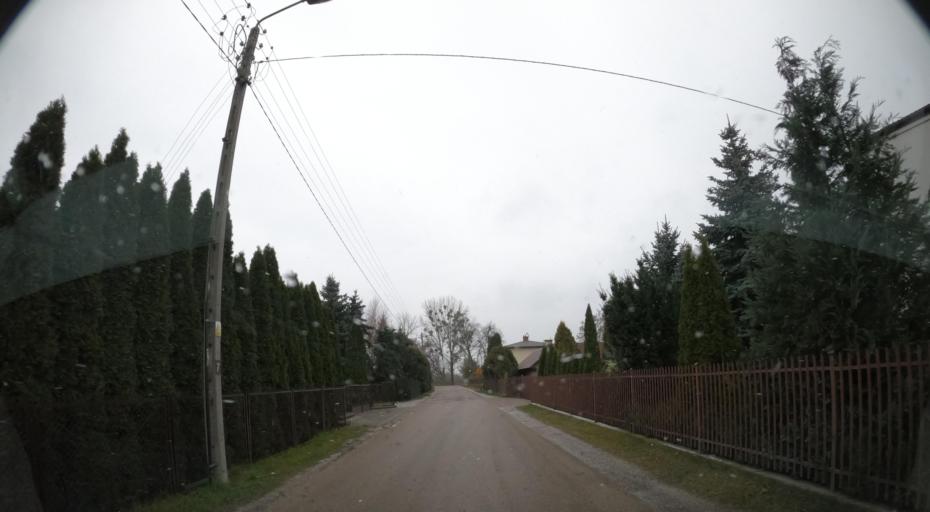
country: PL
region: Masovian Voivodeship
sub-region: Powiat radomski
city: Jedlnia-Letnisko
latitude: 51.3966
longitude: 21.2724
